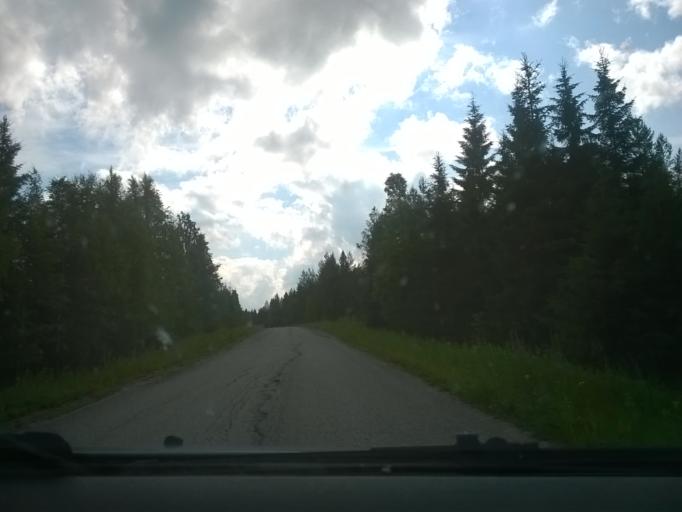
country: FI
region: Kainuu
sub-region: Kehys-Kainuu
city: Kuhmo
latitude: 64.4371
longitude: 29.7084
